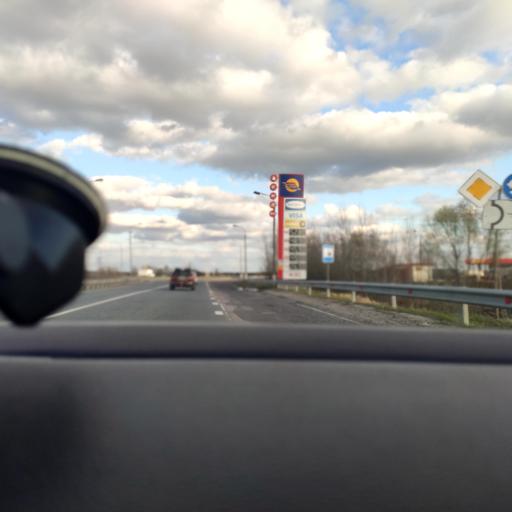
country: RU
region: Moskovskaya
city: Yegor'yevsk
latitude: 55.3904
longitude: 39.0767
